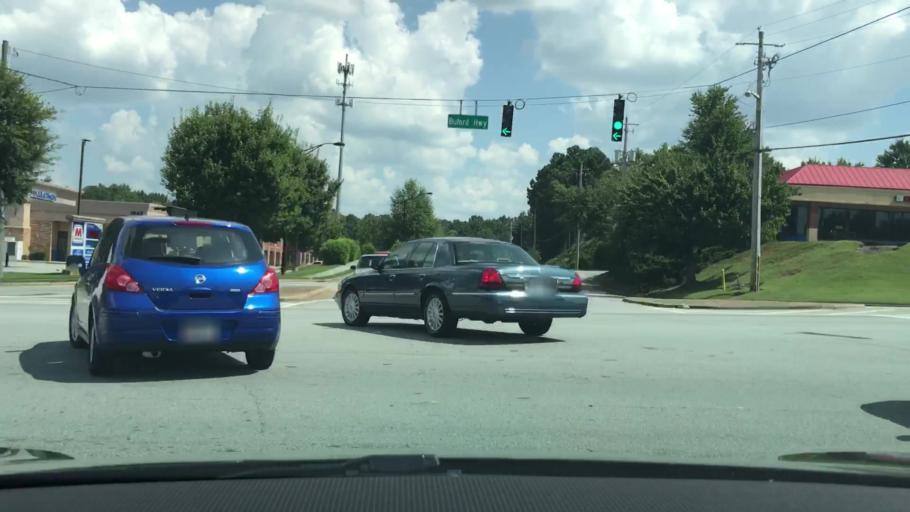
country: US
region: Georgia
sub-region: Gwinnett County
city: Buford
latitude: 34.0995
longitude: -84.0099
